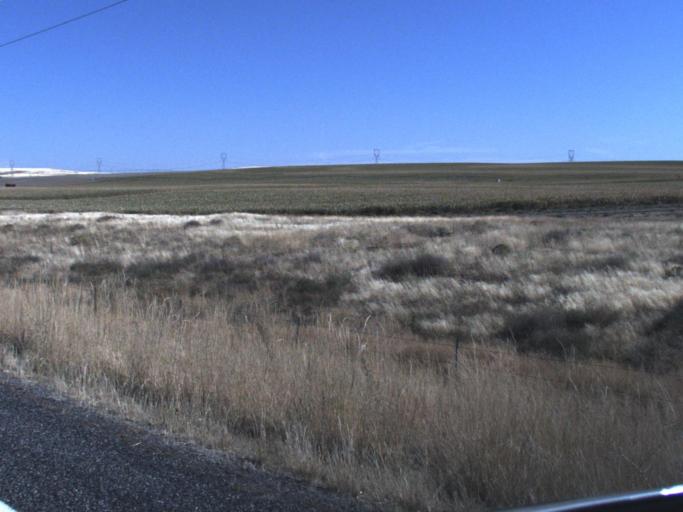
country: US
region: Washington
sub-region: Walla Walla County
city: Burbank
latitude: 46.2821
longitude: -118.7501
